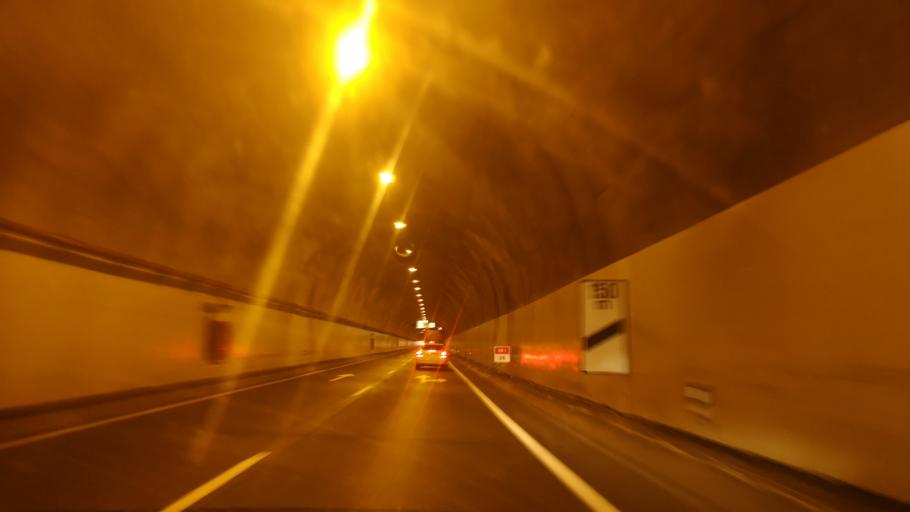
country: PT
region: Madeira
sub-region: Machico
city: Machico
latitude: 32.7094
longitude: -16.7657
